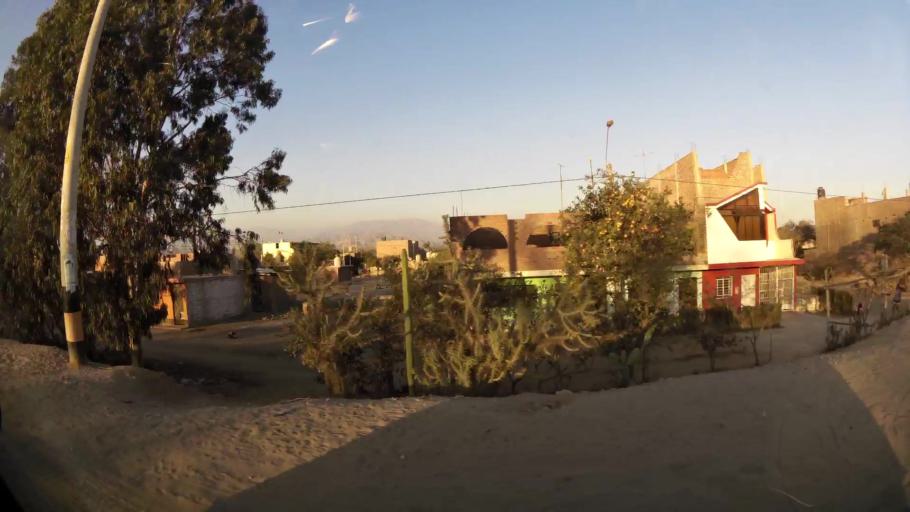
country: PE
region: Ica
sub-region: Provincia de Ica
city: Ica
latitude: -14.0831
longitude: -75.7175
